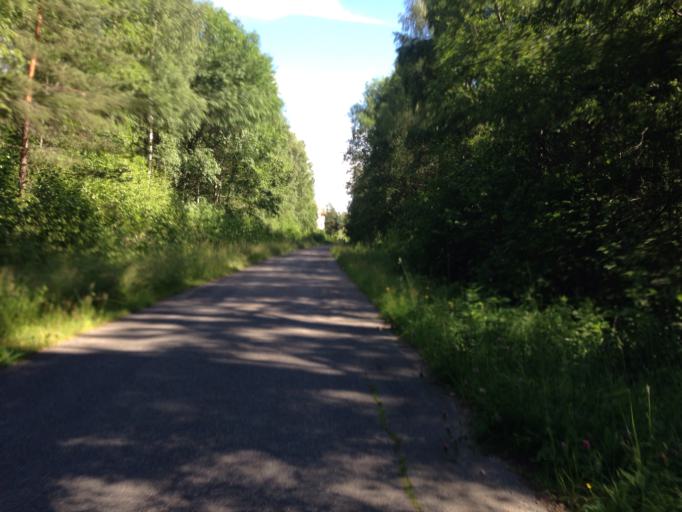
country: SE
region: Dalarna
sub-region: Ludvika Kommun
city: Ludvika
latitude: 60.1875
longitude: 15.1473
